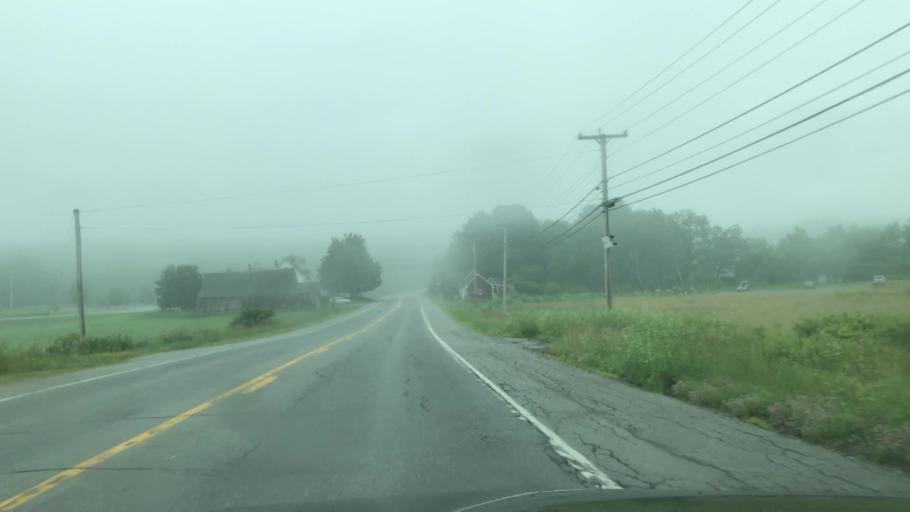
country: US
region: Maine
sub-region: Knox County
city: Rockport
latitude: 44.1867
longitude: -69.0939
